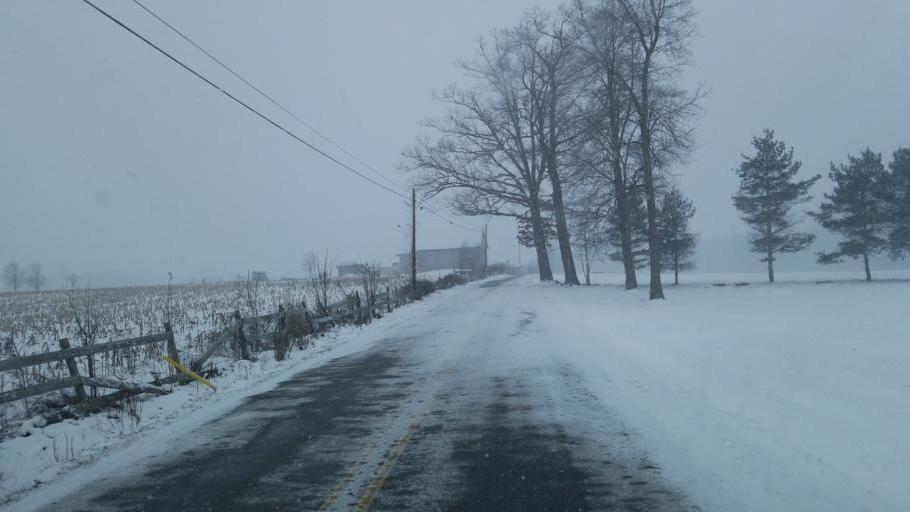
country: US
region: Pennsylvania
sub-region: Crawford County
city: Cochranton
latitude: 41.4473
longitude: -80.0127
